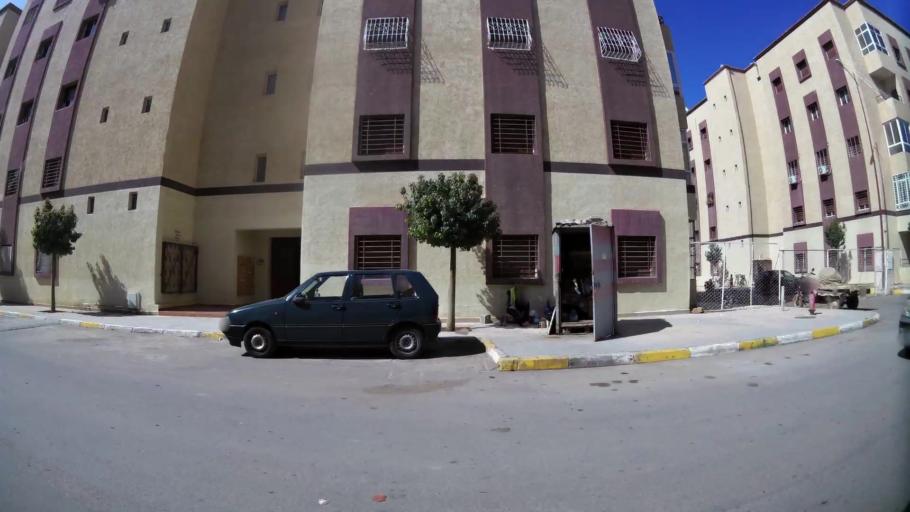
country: MA
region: Oriental
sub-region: Oujda-Angad
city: Oujda
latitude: 34.6989
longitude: -1.8734
